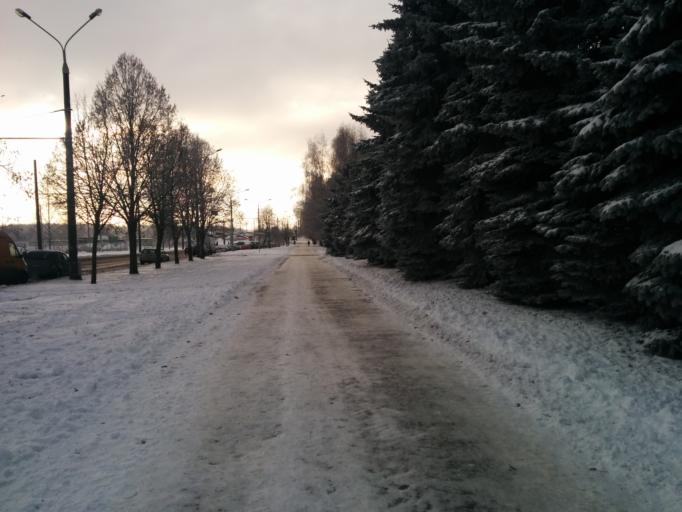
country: BY
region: Minsk
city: Novoye Medvezhino
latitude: 53.9016
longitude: 27.4632
